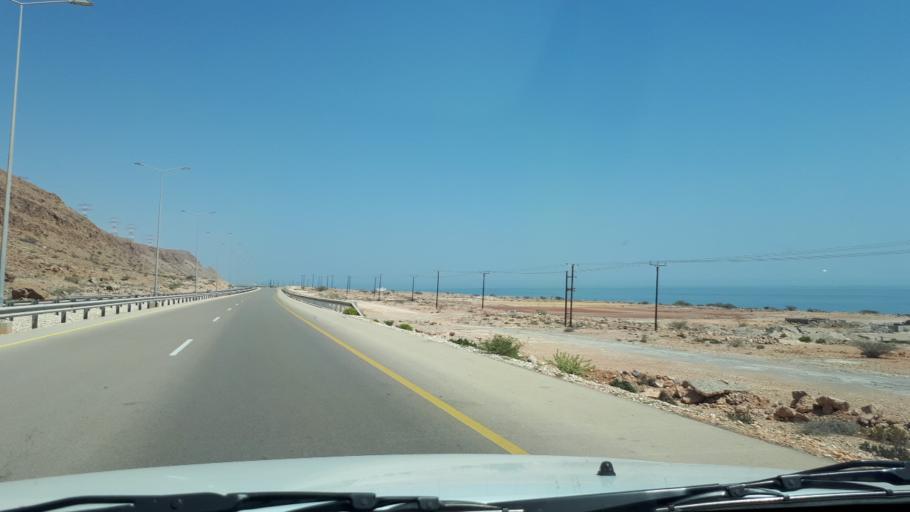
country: OM
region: Ash Sharqiyah
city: Sur
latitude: 22.7943
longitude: 59.2732
